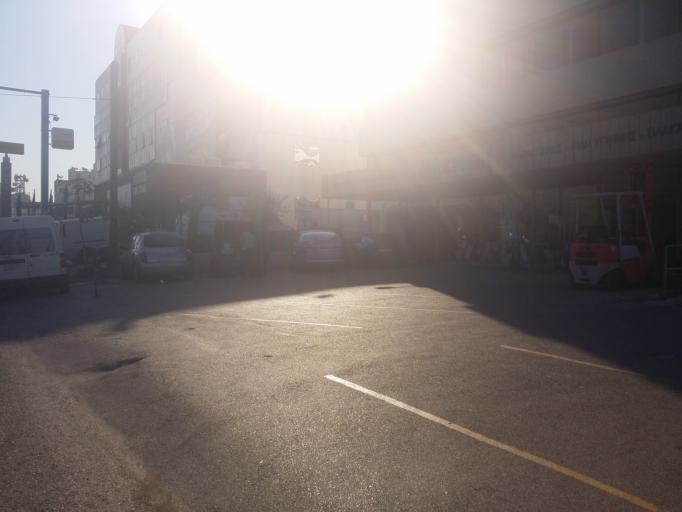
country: GR
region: Attica
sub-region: Nomarchia Athinas
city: Tavros
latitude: 37.9710
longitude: 23.7040
